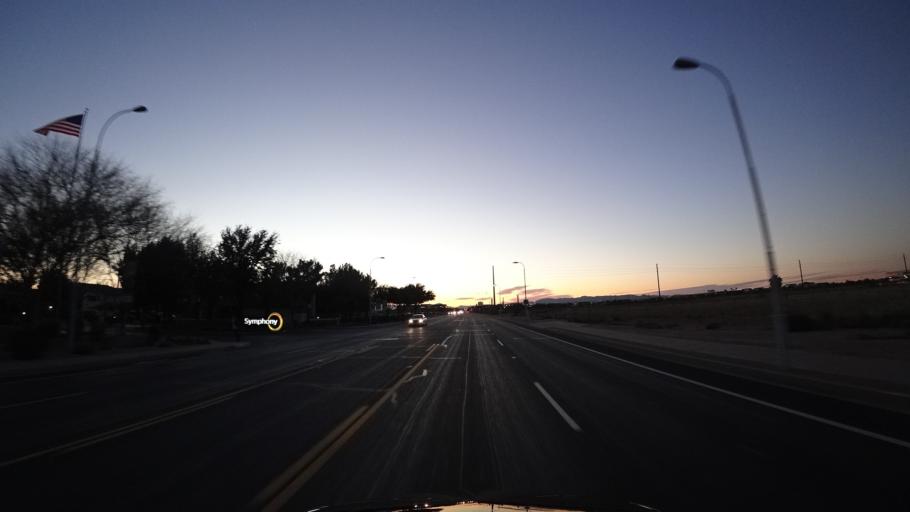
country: US
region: Arizona
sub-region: Maricopa County
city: Chandler
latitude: 33.2987
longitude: -111.8792
